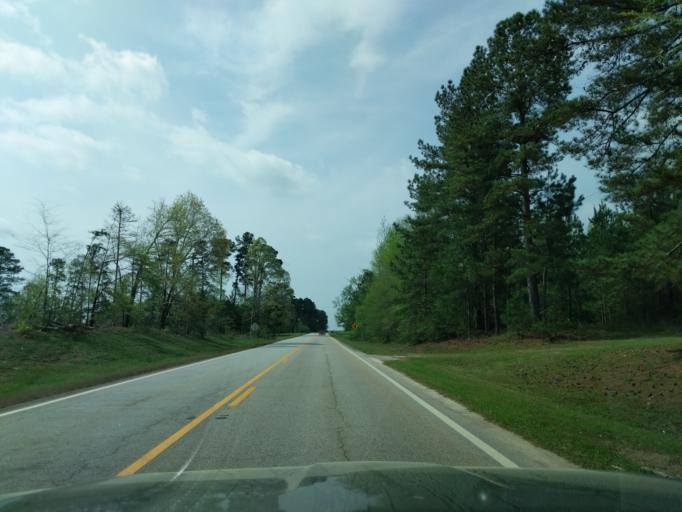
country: US
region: Georgia
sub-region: Lincoln County
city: Lincolnton
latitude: 33.7685
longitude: -82.3751
